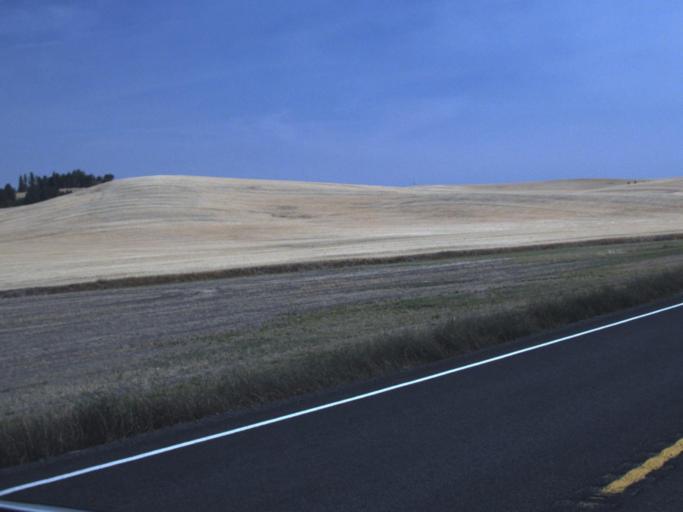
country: US
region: Washington
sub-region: Whitman County
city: Pullman
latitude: 46.7949
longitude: -117.1416
